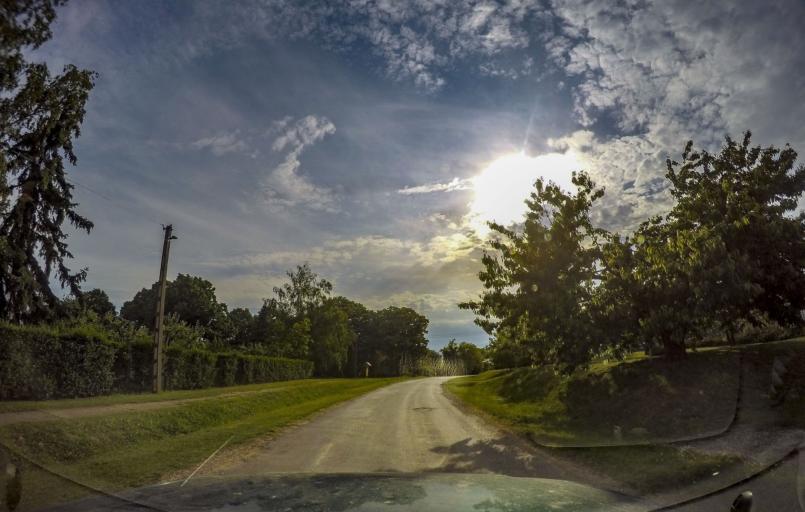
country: HU
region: Somogy
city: Karad
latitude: 46.6944
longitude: 17.8443
